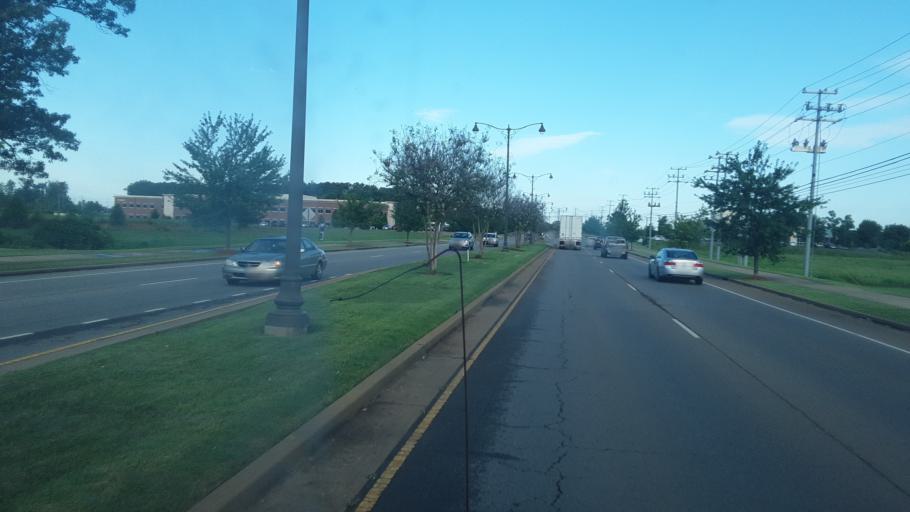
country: US
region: Tennessee
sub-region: Montgomery County
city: Clarksville
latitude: 36.5799
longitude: -87.2731
